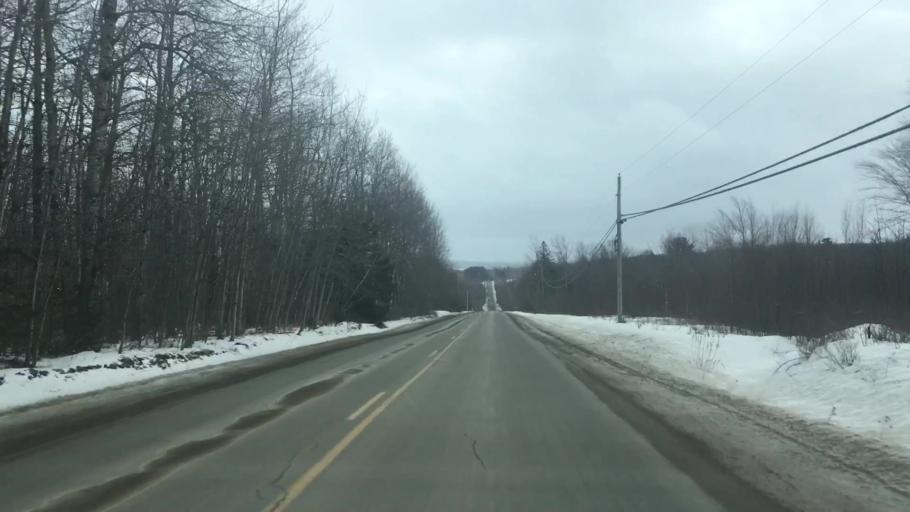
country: US
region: Maine
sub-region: Washington County
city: East Machias
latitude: 44.9732
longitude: -67.4494
